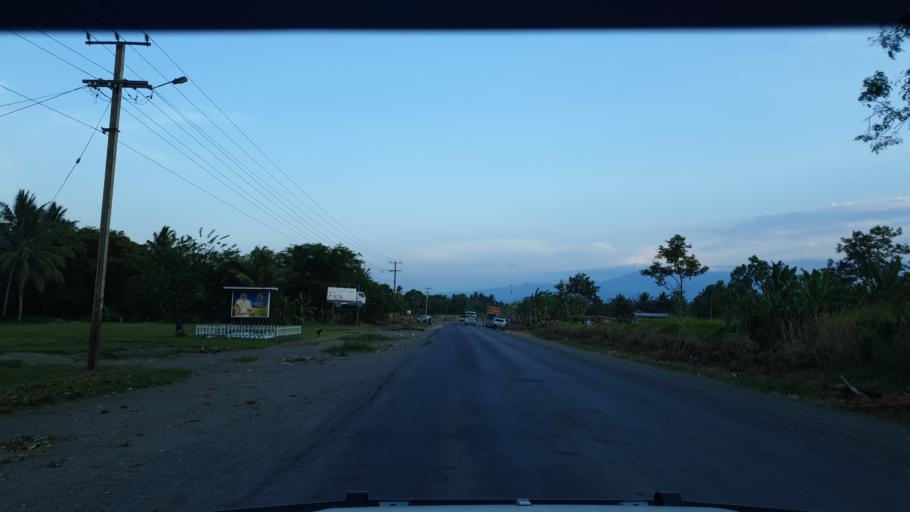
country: PG
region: Morobe
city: Lae
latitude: -6.5775
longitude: 146.7705
